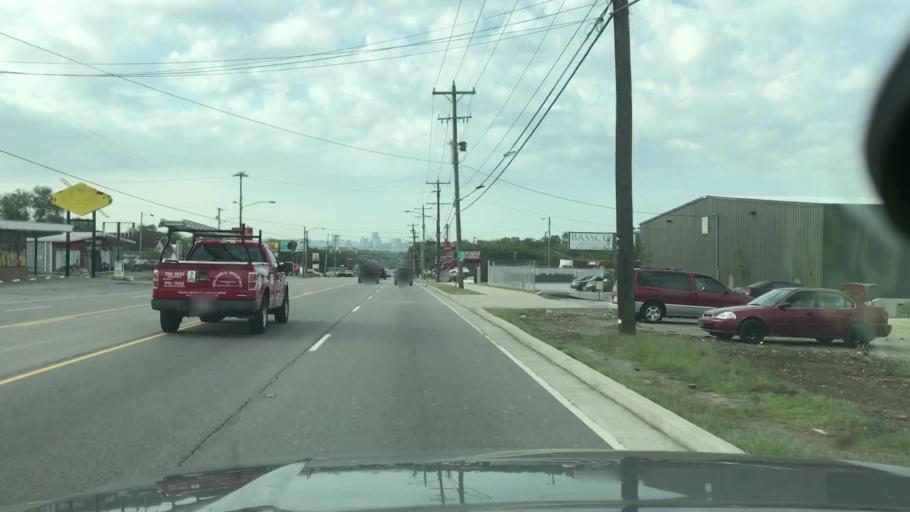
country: US
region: Tennessee
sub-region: Davidson County
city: Nashville
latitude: 36.2234
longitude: -86.7612
